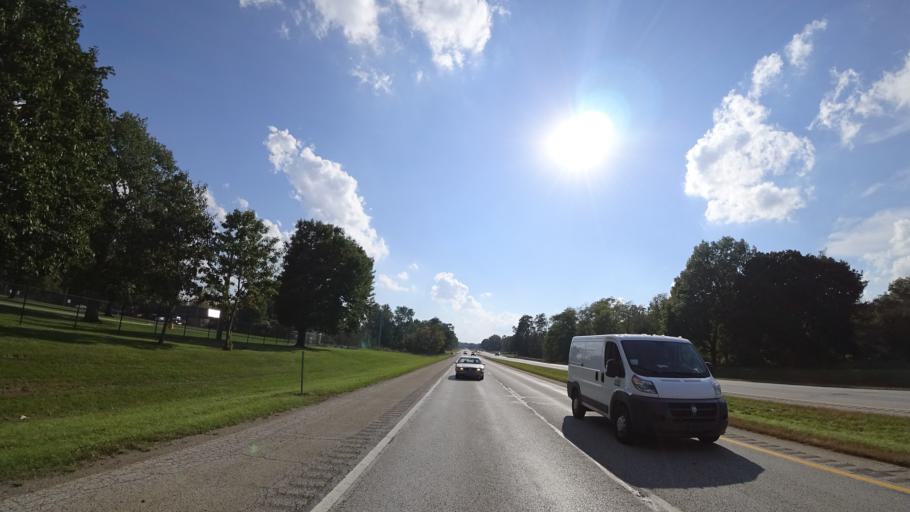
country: US
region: Michigan
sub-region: Saint Joseph County
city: Three Rivers
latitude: 41.9562
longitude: -85.6452
